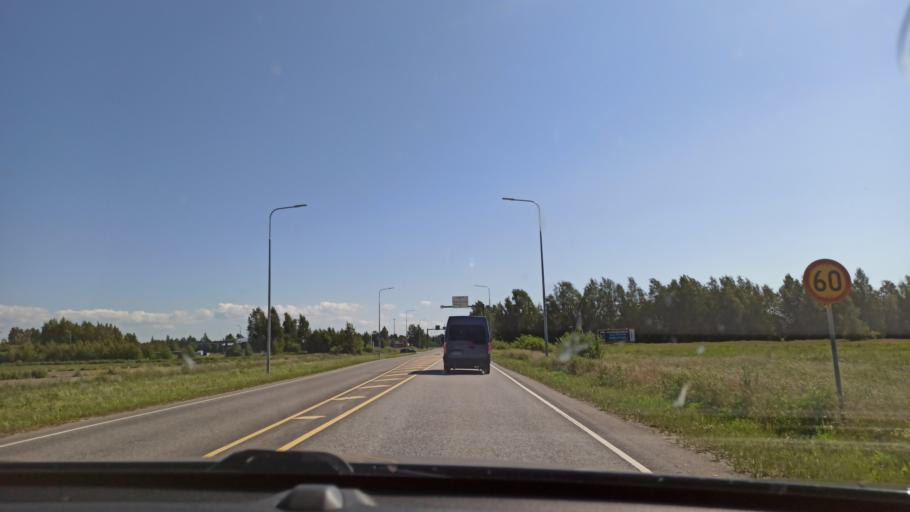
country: FI
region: Satakunta
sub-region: Pori
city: Pori
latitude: 61.5145
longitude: 21.8032
